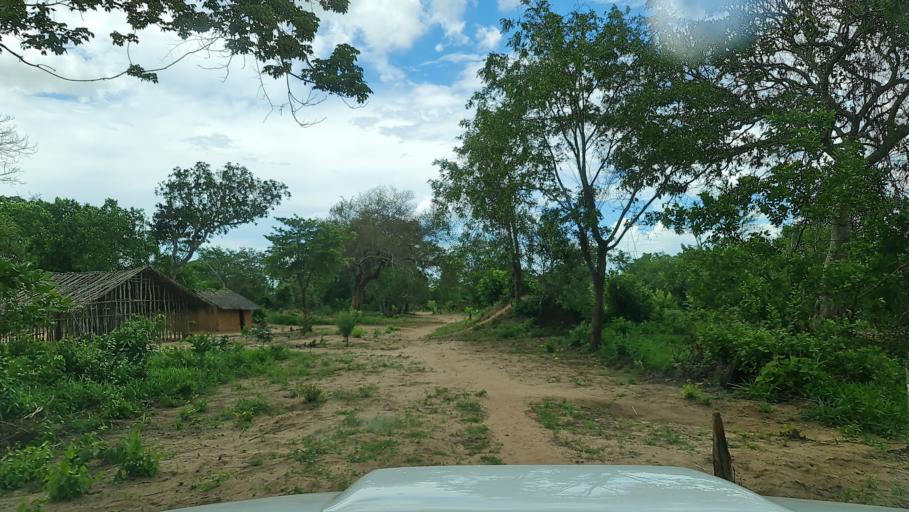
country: MZ
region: Nampula
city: Ilha de Mocambique
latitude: -15.4975
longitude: 40.1661
